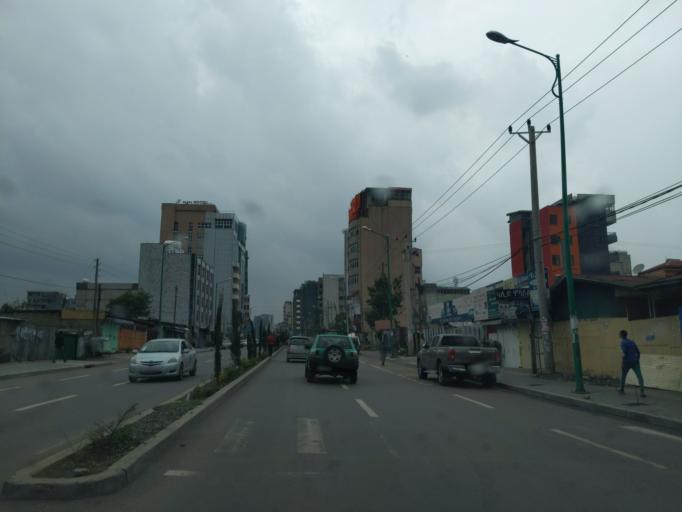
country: ET
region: Adis Abeba
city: Addis Ababa
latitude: 8.9917
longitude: 38.7662
